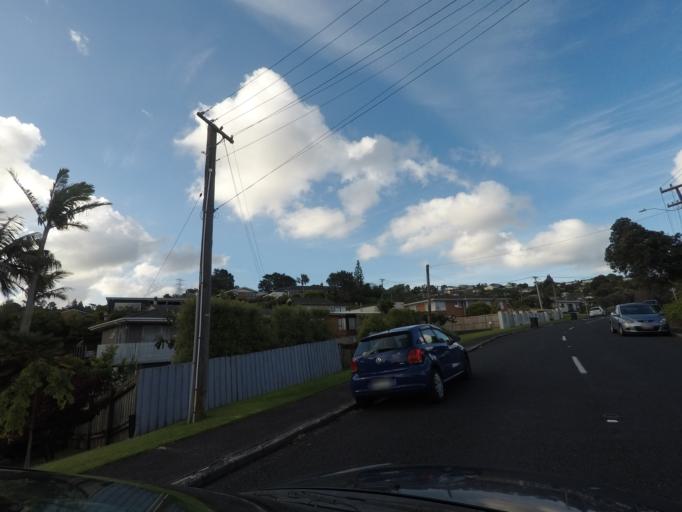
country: NZ
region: Auckland
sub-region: Auckland
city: Mangere
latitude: -36.9270
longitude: 174.7598
